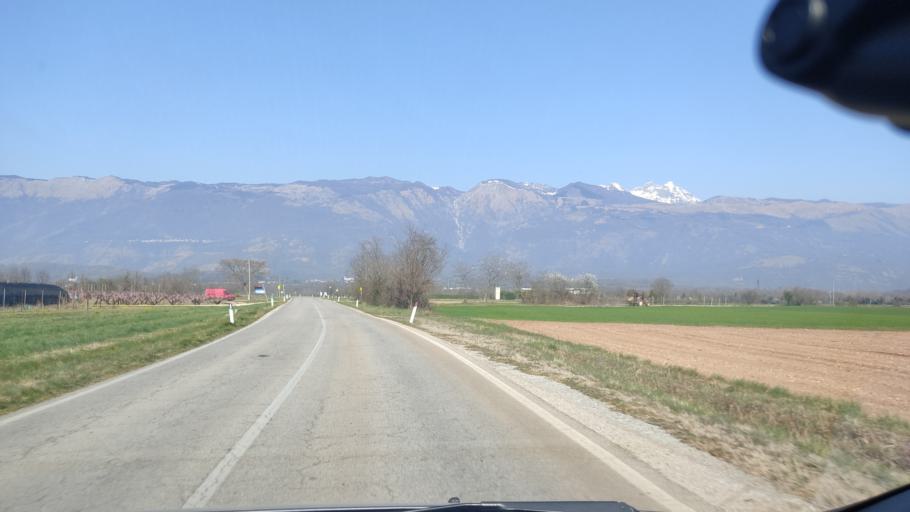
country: IT
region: Friuli Venezia Giulia
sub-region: Provincia di Pordenone
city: Budoia
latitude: 46.0246
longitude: 12.5640
